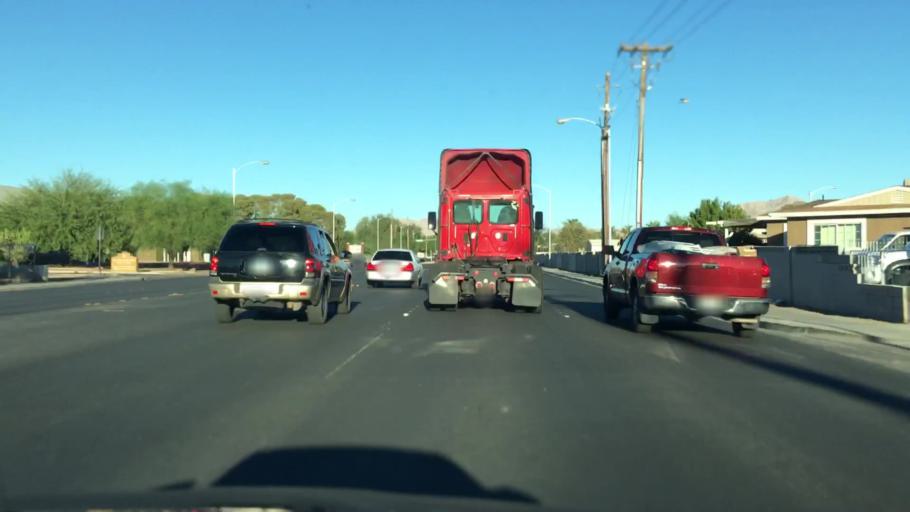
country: US
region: Nevada
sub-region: Clark County
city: North Las Vegas
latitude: 36.2176
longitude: -115.1104
